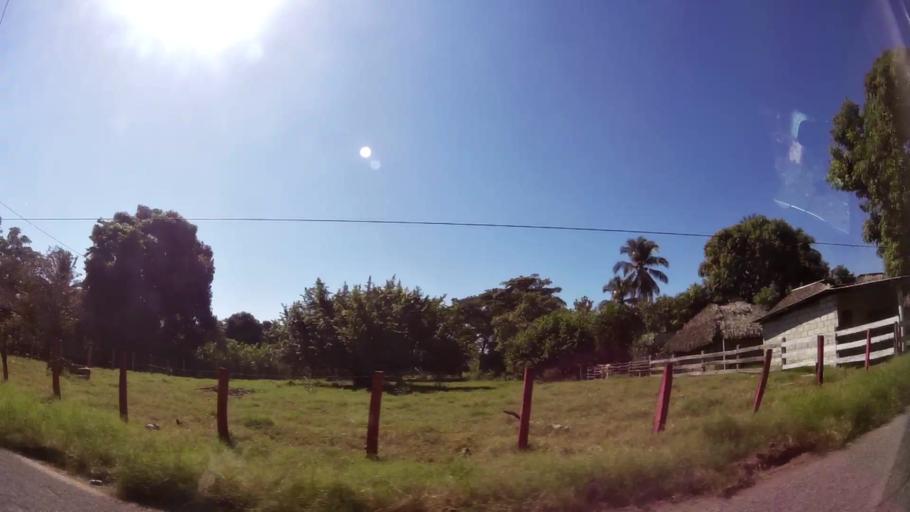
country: GT
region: Escuintla
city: Iztapa
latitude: 13.9214
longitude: -90.5689
